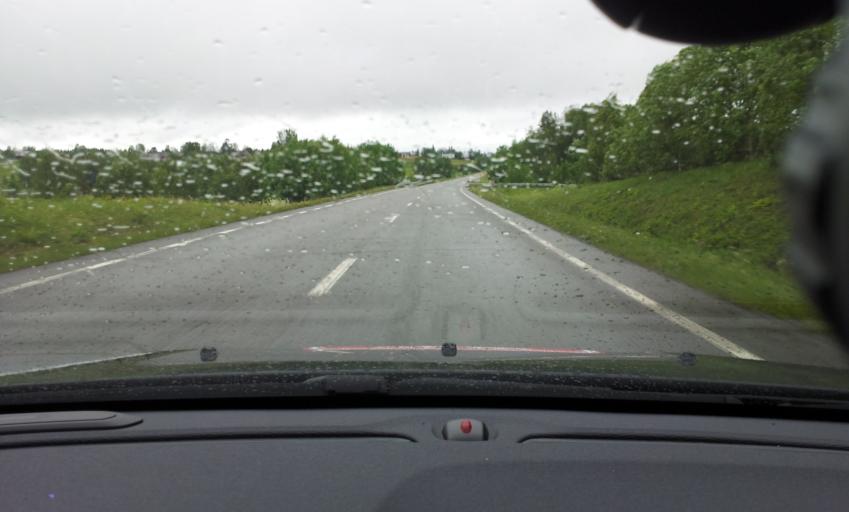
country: SE
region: Jaemtland
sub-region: Krokoms Kommun
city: Krokom
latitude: 63.5129
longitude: 14.5226
